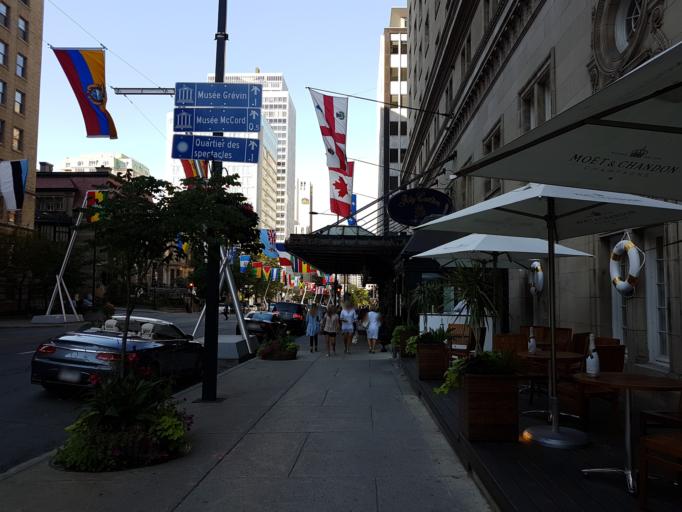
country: CA
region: Quebec
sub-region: Montreal
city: Montreal
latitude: 45.5000
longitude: -73.5783
